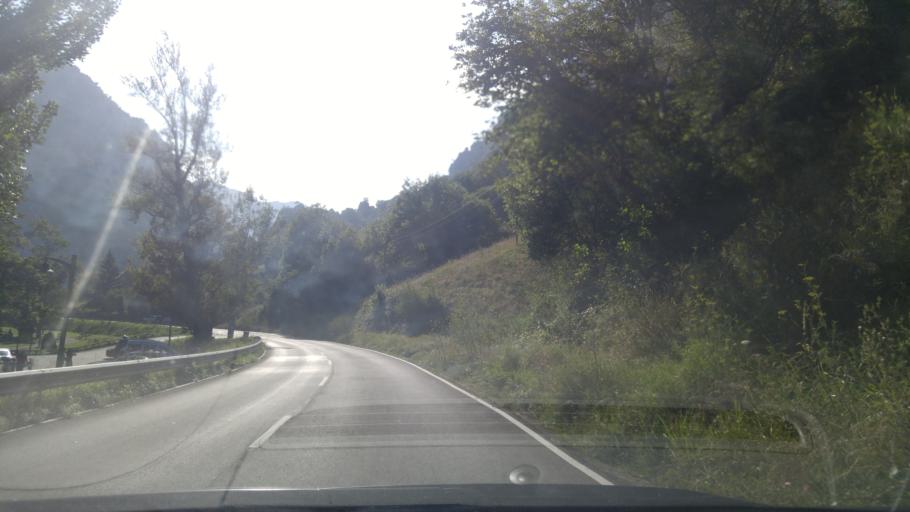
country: ES
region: Asturias
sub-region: Province of Asturias
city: Proaza
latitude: 43.2009
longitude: -6.0126
